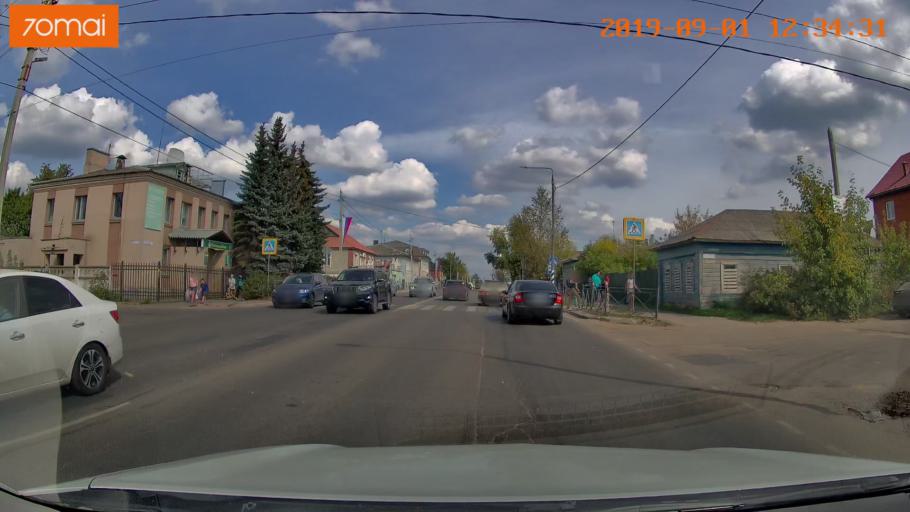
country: RU
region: Kaluga
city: Maloyaroslavets
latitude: 55.0100
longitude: 36.4547
